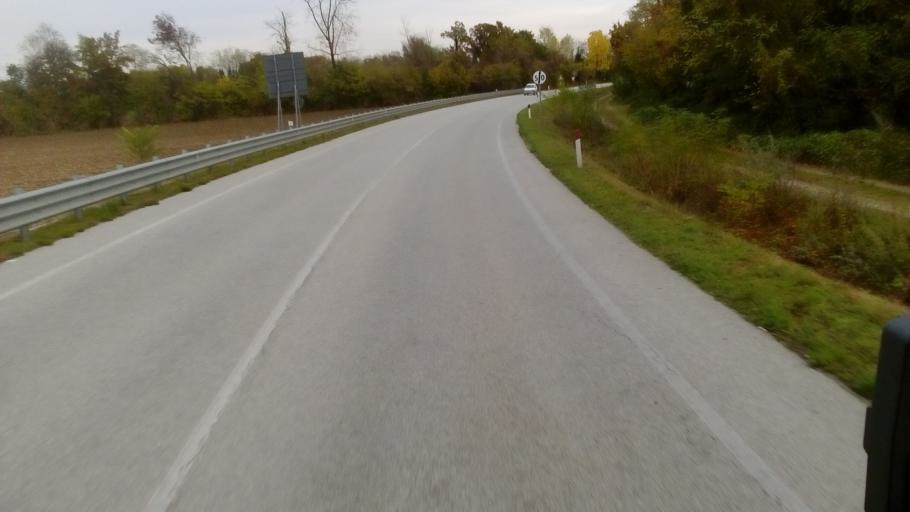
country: IT
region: Friuli Venezia Giulia
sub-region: Provincia di Pordenone
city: Vivaro
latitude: 46.0950
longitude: 12.7935
